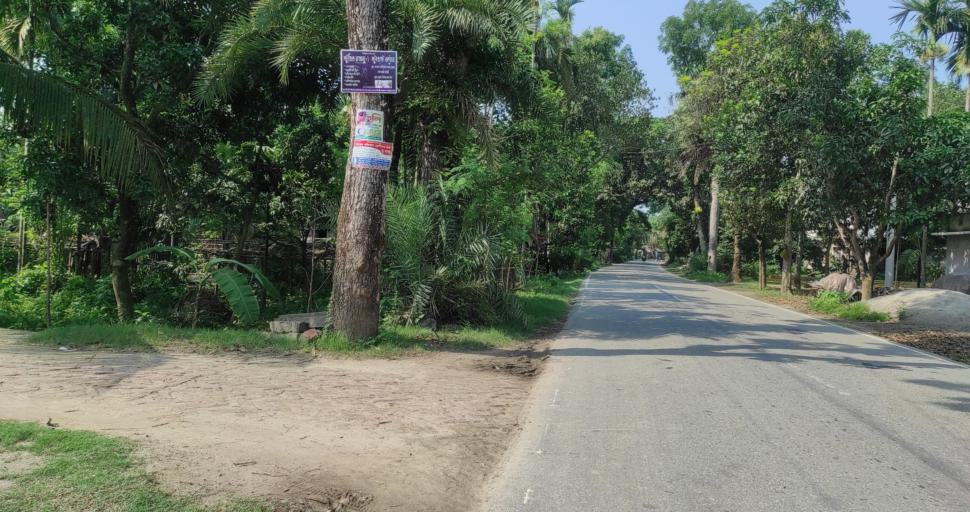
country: BD
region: Rajshahi
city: Ishurdi
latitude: 24.2593
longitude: 89.0488
